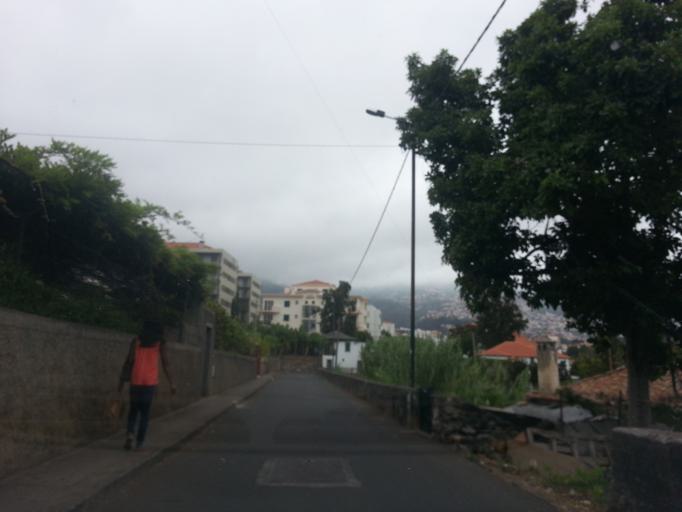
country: PT
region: Madeira
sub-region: Funchal
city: Funchal
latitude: 32.6477
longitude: -16.9295
